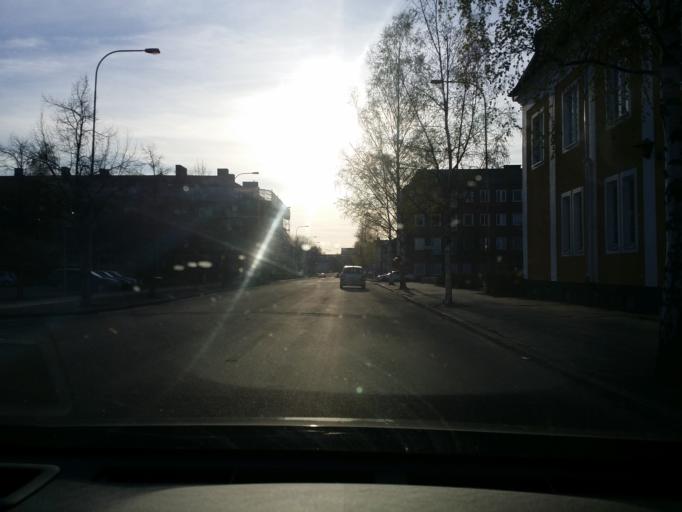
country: SE
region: Dalarna
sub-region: Avesta Kommun
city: Avesta
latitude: 60.1443
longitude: 16.1676
